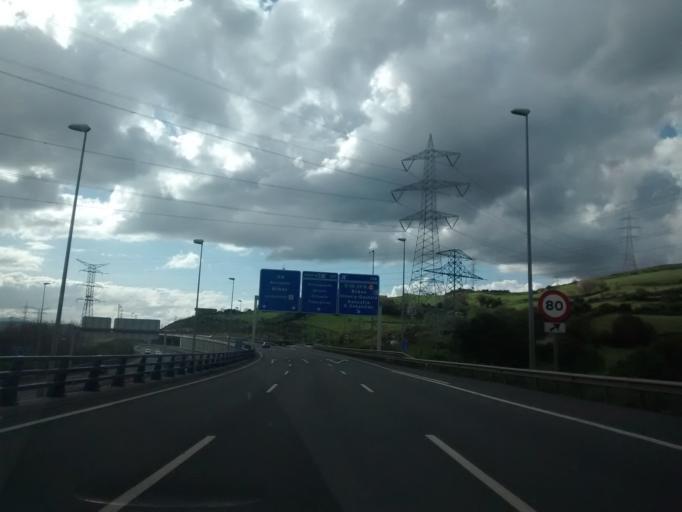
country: ES
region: Basque Country
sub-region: Bizkaia
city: Urtuella
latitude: 43.3165
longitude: -3.0488
